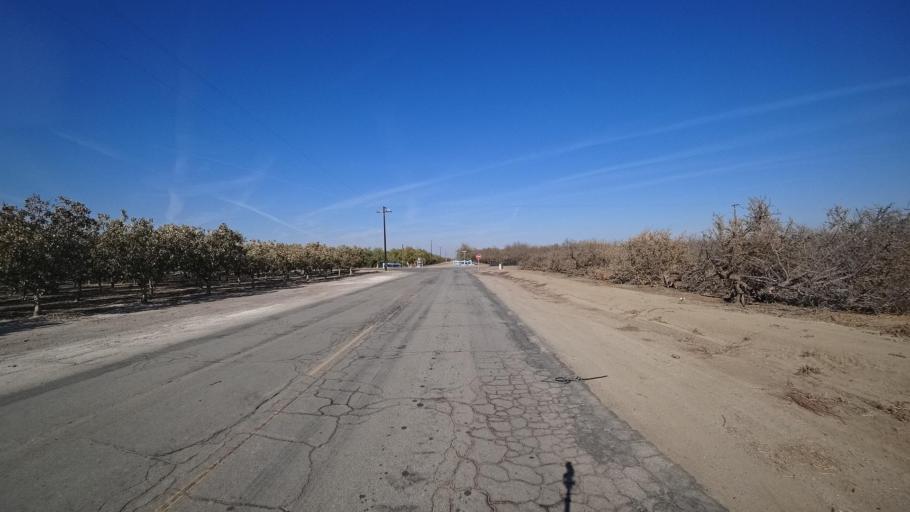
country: US
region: California
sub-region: Kern County
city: Wasco
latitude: 35.6661
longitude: -119.3485
